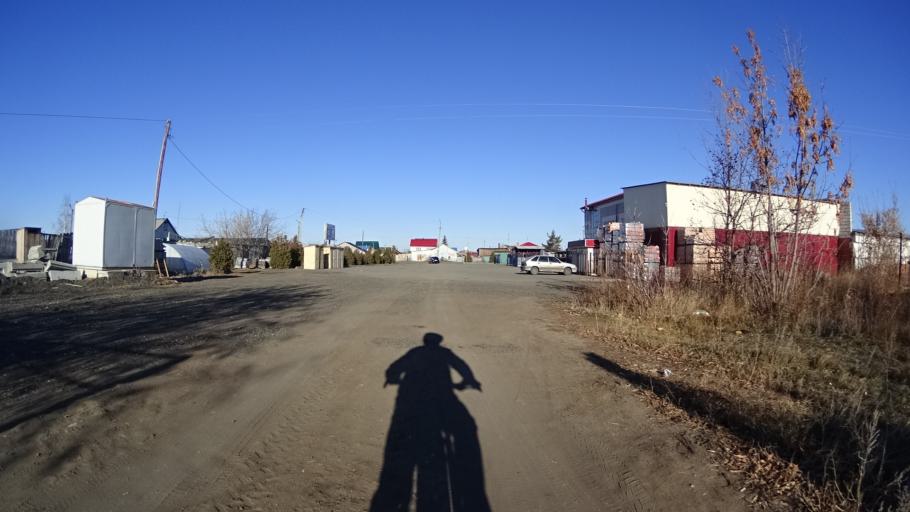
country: RU
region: Chelyabinsk
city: Troitsk
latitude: 54.0827
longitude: 61.5104
